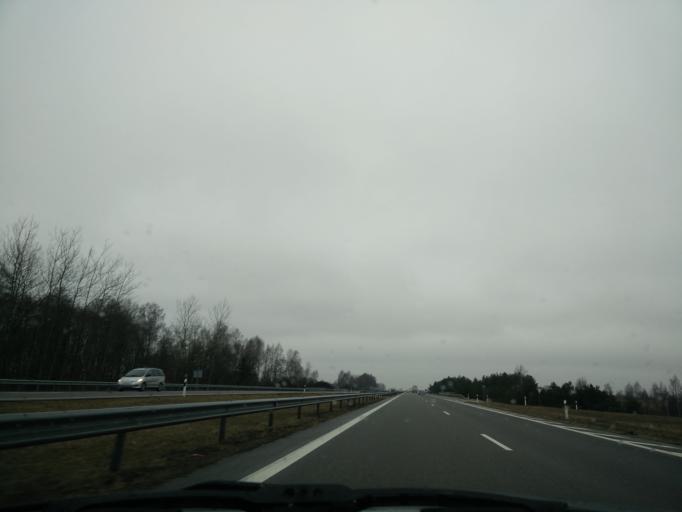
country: LT
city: Kelme
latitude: 55.3968
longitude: 22.8677
